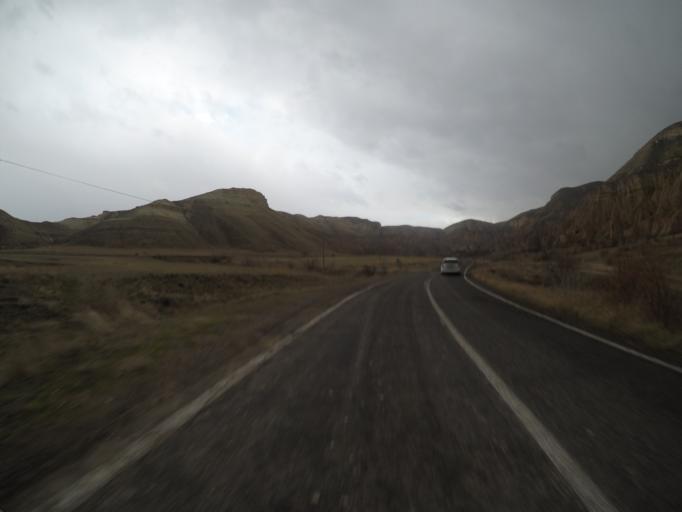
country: TR
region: Nevsehir
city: Goereme
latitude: 38.6756
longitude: 34.8615
